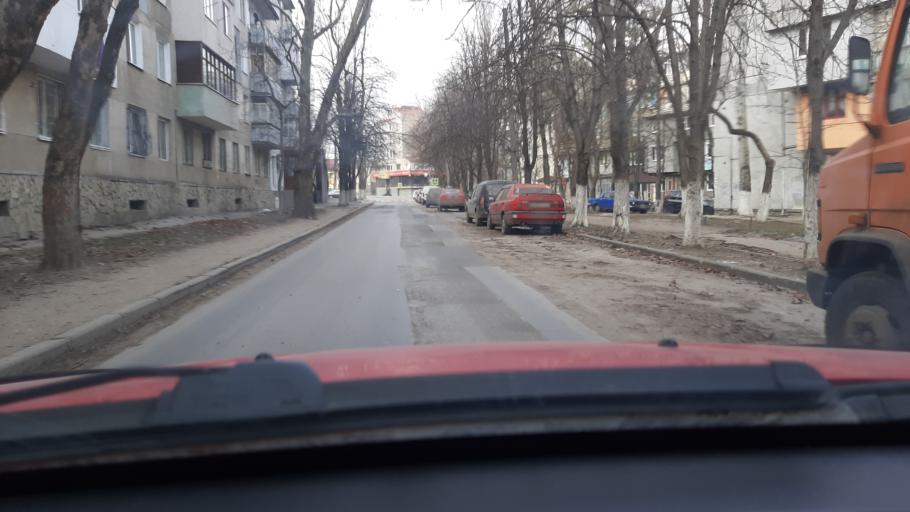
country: MD
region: Chisinau
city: Chisinau
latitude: 47.0315
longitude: 28.7928
